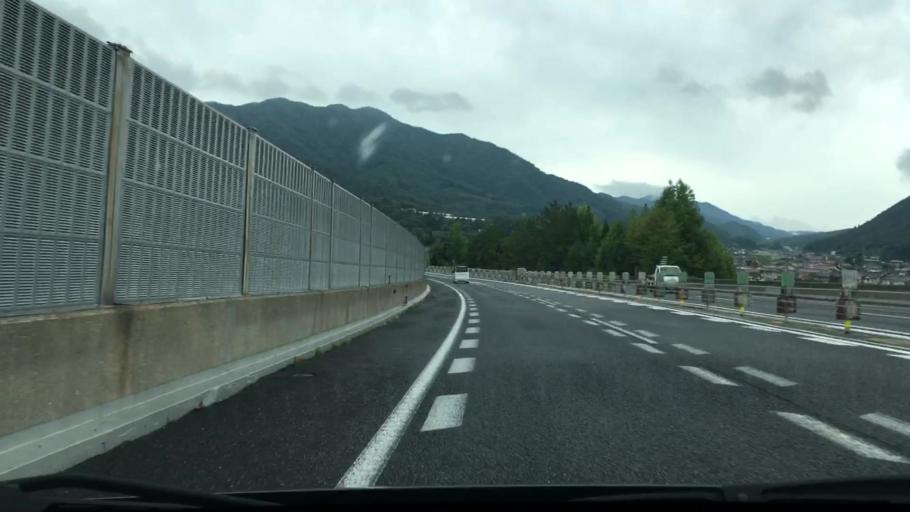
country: JP
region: Hiroshima
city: Hiroshima-shi
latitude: 34.6490
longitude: 132.5168
